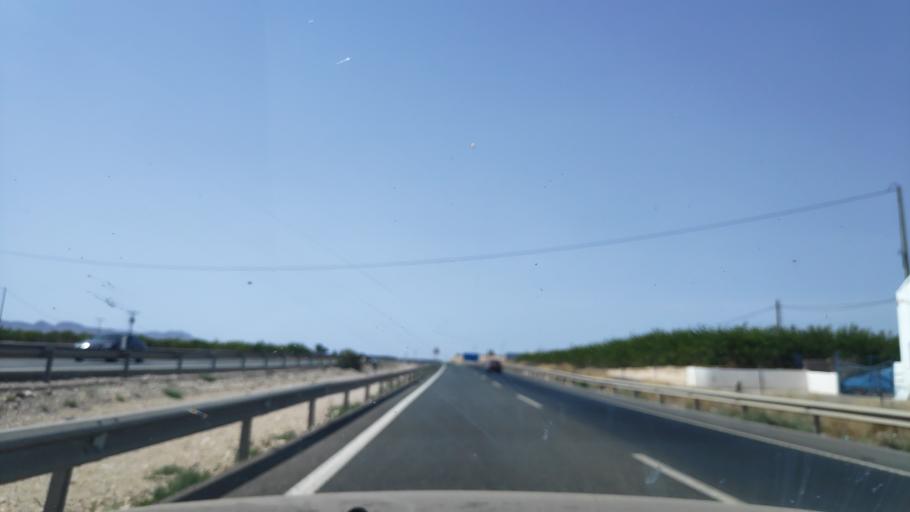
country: ES
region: Murcia
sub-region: Murcia
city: Lorqui
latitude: 38.1139
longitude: -1.2404
